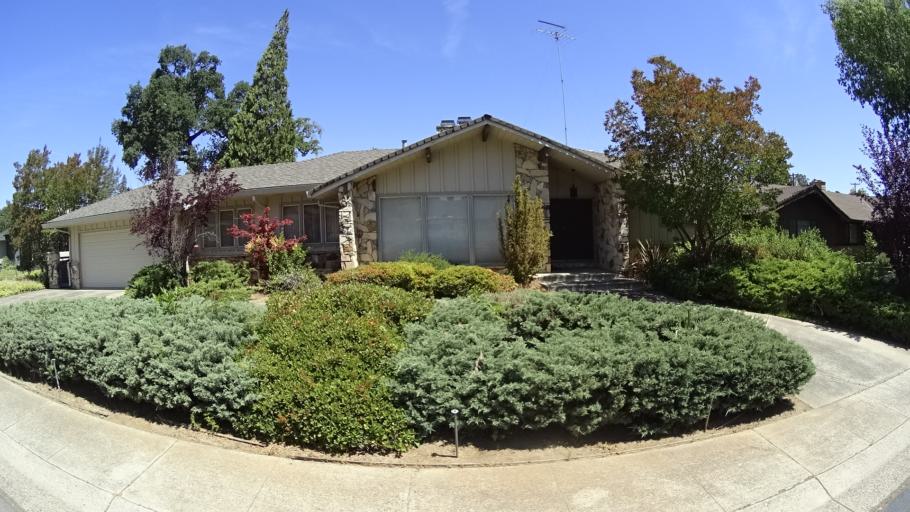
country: US
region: California
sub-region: Sacramento County
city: Parkway
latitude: 38.5166
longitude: -121.5128
